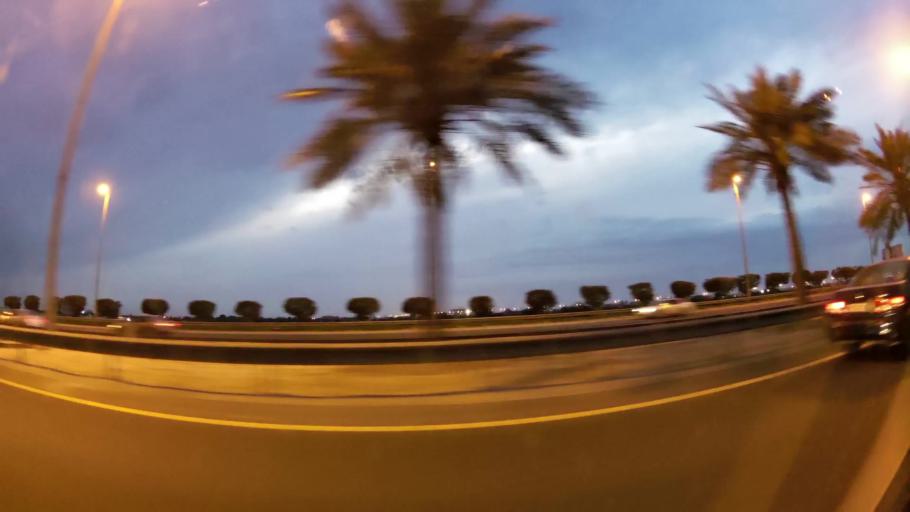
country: BH
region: Northern
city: Madinat `Isa
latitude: 26.1753
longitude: 50.5024
